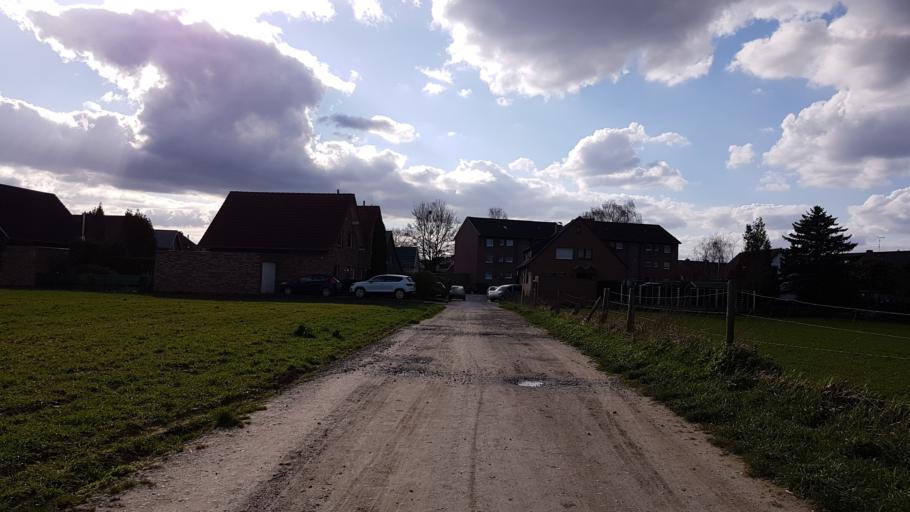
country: DE
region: North Rhine-Westphalia
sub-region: Regierungsbezirk Dusseldorf
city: Schwalmtal
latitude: 51.2255
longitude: 6.2485
